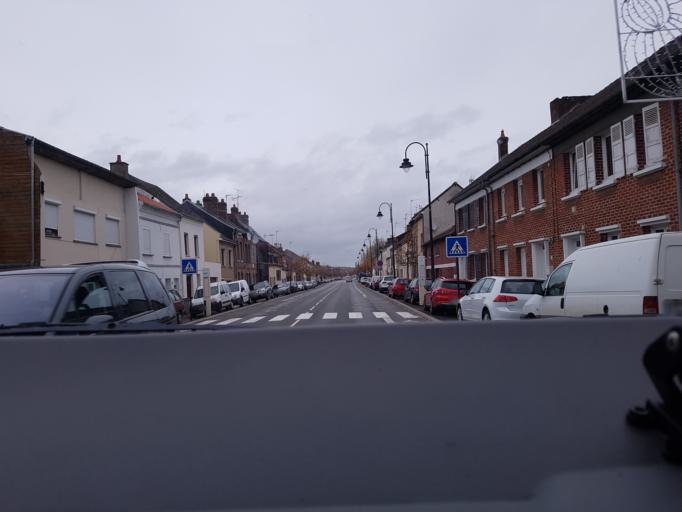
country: FR
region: Picardie
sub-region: Departement de la Somme
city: Abbeville
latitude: 50.1060
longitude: 1.8008
